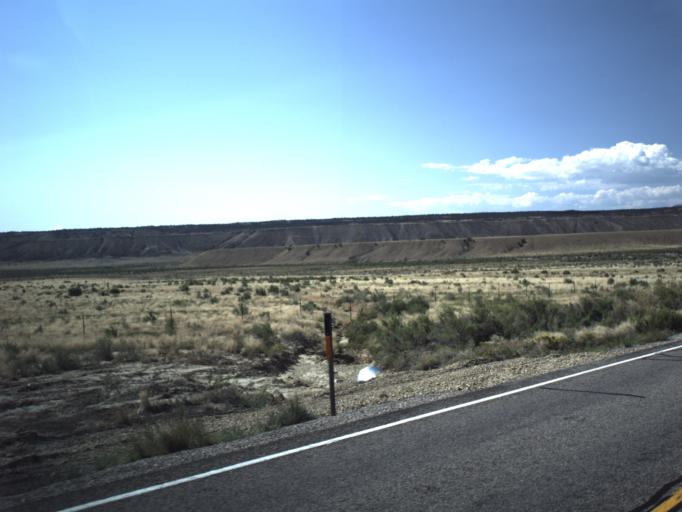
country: US
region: Utah
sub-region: Emery County
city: Ferron
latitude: 38.8220
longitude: -111.3273
